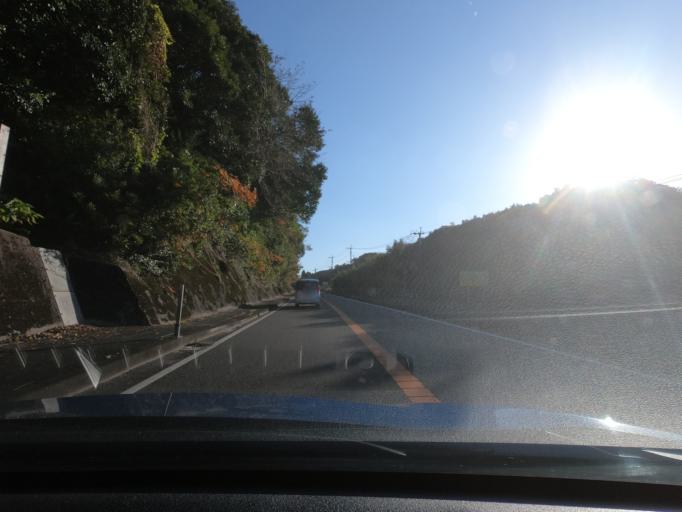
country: JP
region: Kagoshima
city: Akune
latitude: 32.0555
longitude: 130.2213
